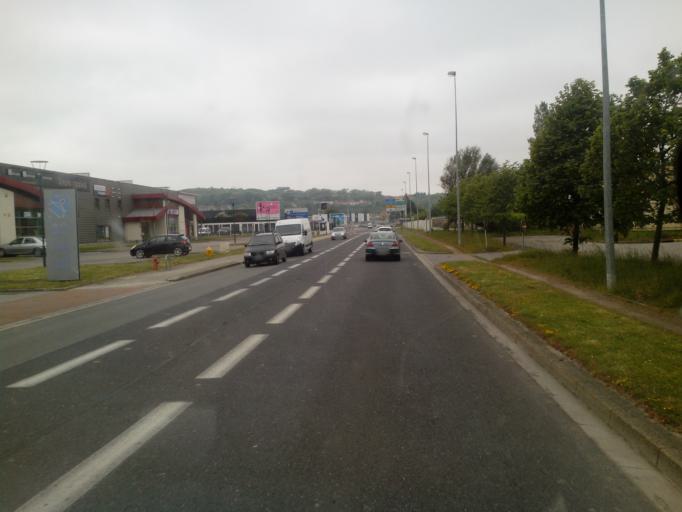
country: FR
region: Nord-Pas-de-Calais
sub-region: Departement du Pas-de-Calais
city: Saint-Leonard
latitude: 50.6907
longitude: 1.6157
